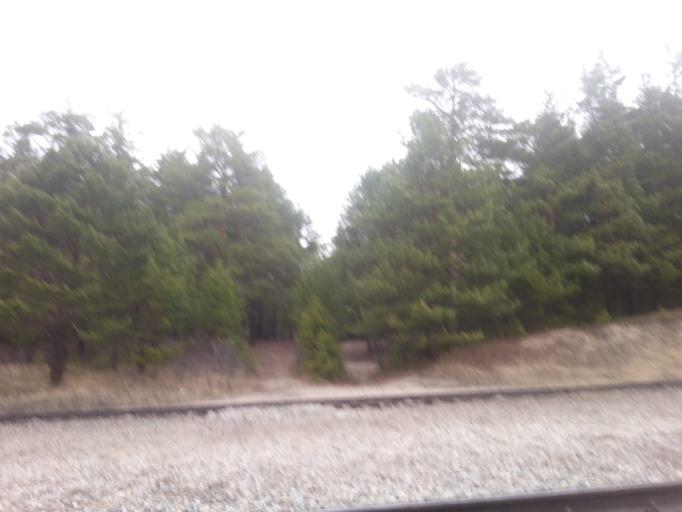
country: RU
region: Altai Krai
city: Yuzhnyy
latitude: 53.3146
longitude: 83.6894
